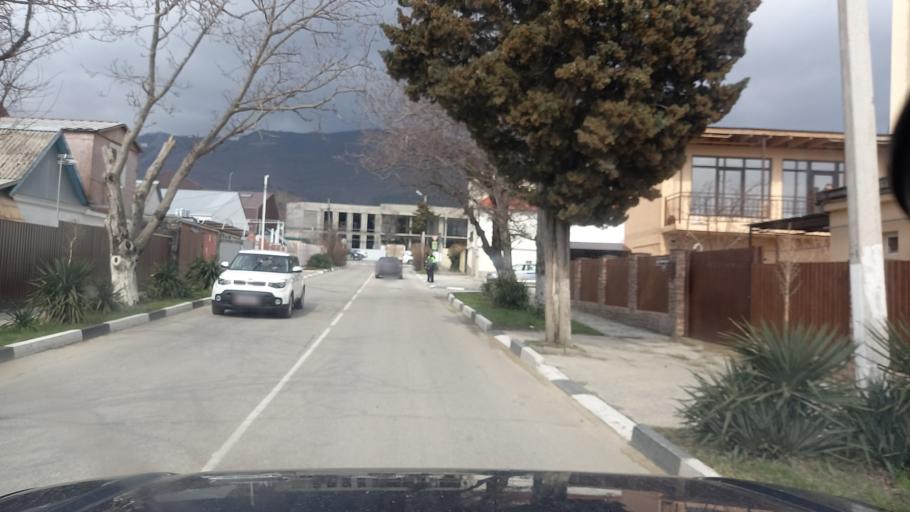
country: RU
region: Krasnodarskiy
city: Gelendzhik
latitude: 44.5602
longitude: 38.0921
